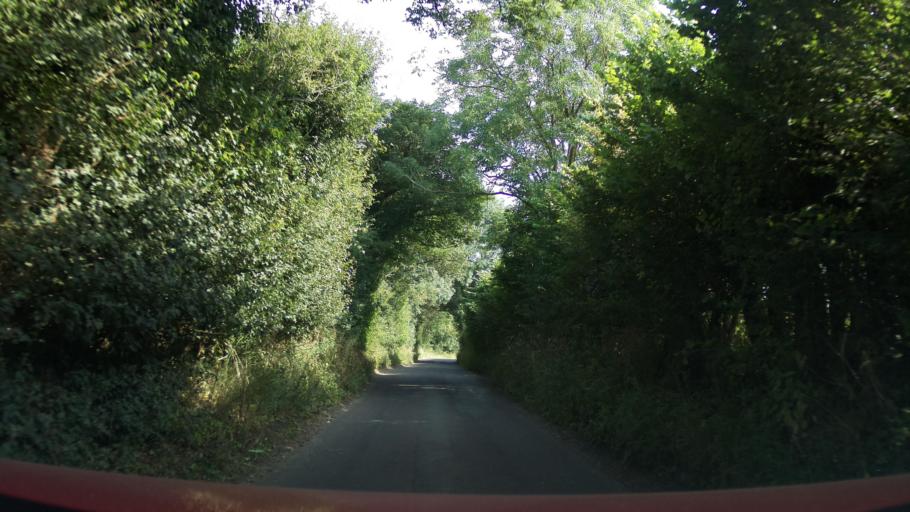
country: GB
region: England
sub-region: Wiltshire
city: Minety
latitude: 51.6252
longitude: -1.9705
